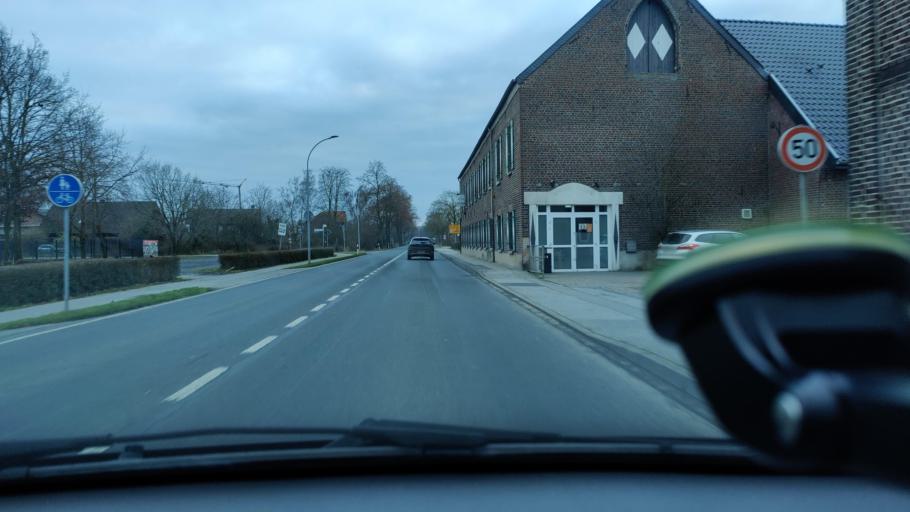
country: DE
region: North Rhine-Westphalia
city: Geldern
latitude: 51.4899
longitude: 6.2980
